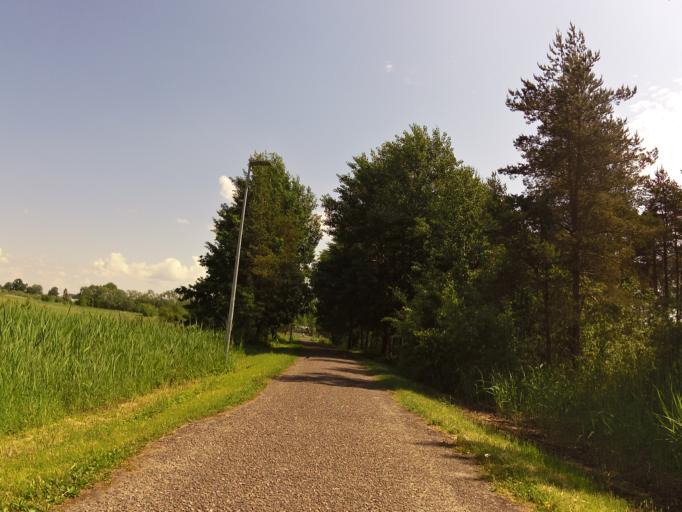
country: EE
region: Laeaene
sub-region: Haapsalu linn
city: Haapsalu
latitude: 58.9391
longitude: 23.5247
